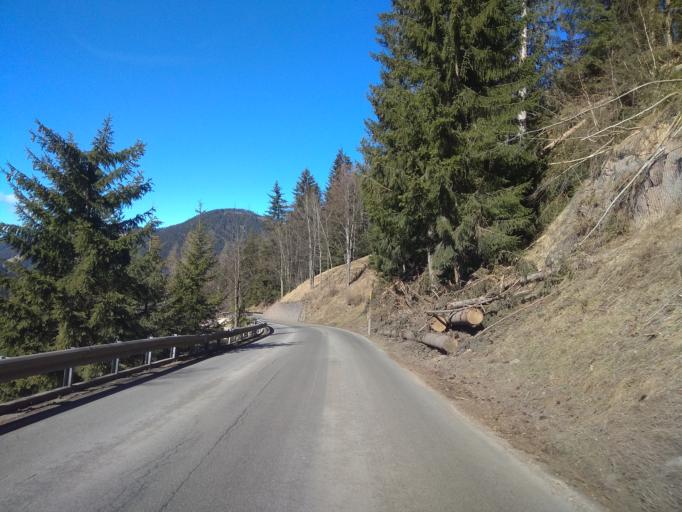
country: IT
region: Trentino-Alto Adige
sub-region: Bolzano
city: Nova Levante
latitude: 46.4184
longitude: 11.5657
